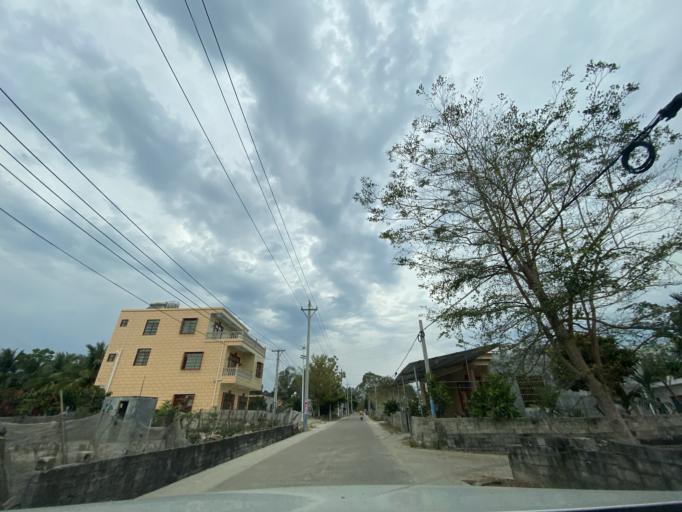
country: CN
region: Hainan
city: Yingzhou
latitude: 18.4183
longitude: 109.8228
